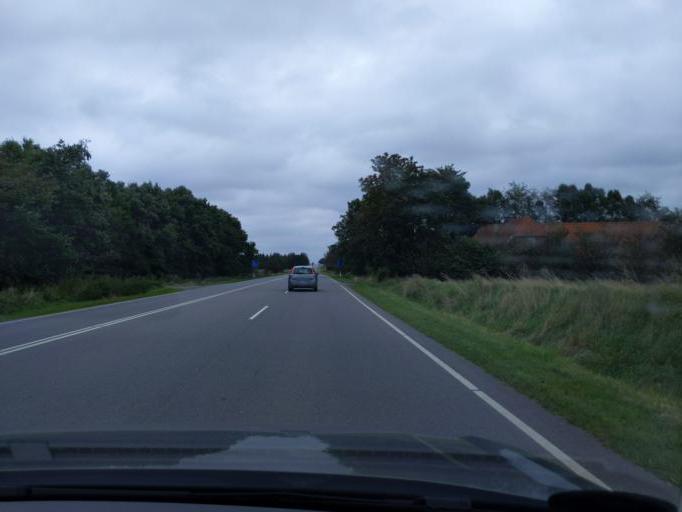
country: DK
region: North Denmark
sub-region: Mariagerfjord Kommune
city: Hobro
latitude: 56.5740
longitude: 9.8162
